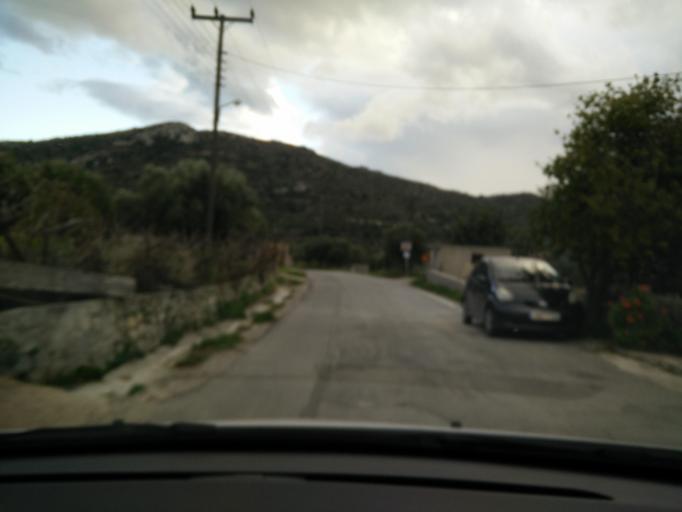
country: GR
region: Crete
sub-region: Nomos Lasithiou
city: Kritsa
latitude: 35.0931
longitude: 25.6869
